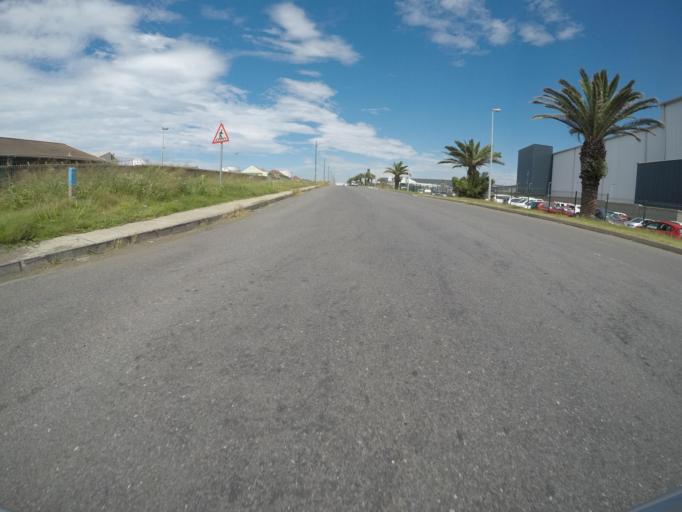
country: ZA
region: Eastern Cape
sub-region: Buffalo City Metropolitan Municipality
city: East London
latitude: -33.0297
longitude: 27.8991
